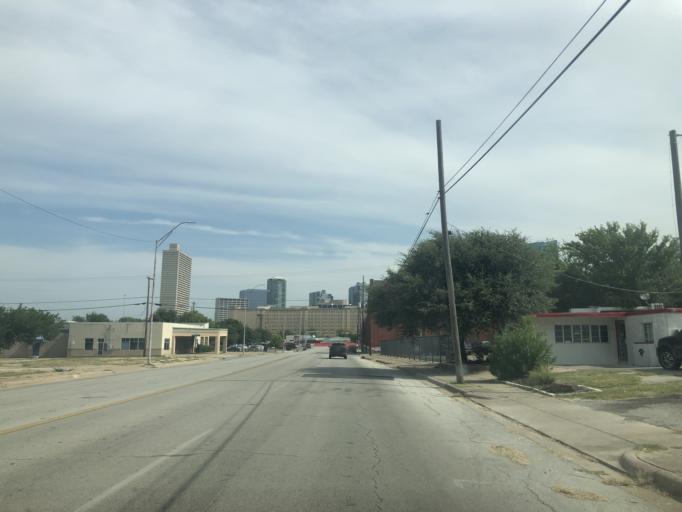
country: US
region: Texas
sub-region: Tarrant County
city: Fort Worth
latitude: 32.7412
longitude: -97.3316
